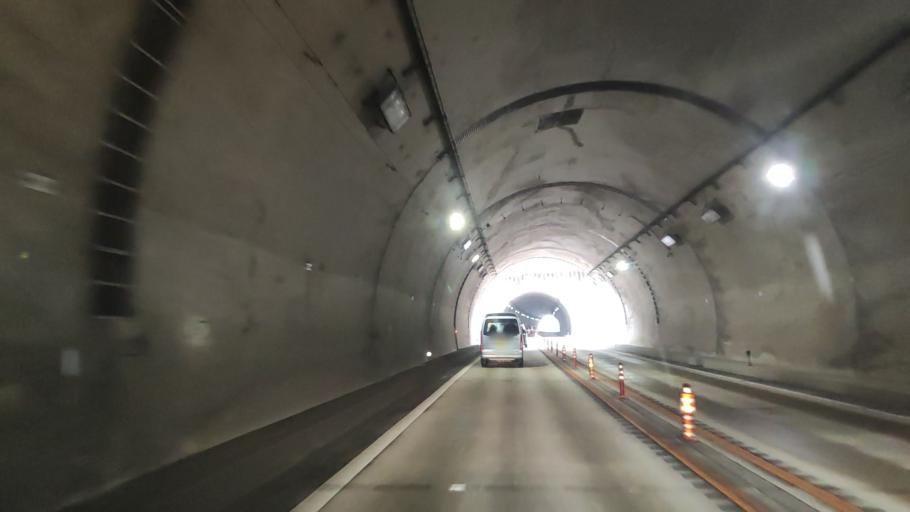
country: JP
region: Tokushima
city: Kamojimacho-jogejima
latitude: 34.1090
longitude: 134.3159
